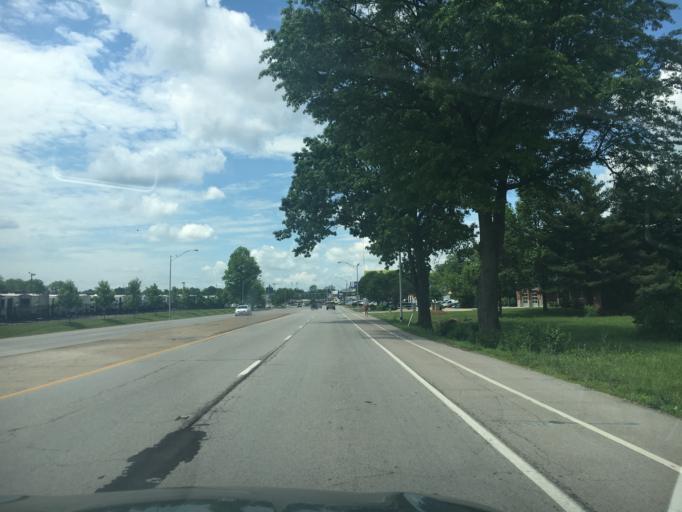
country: US
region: Kentucky
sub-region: Fayette County
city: Lexington-Fayette
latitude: 38.0700
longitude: -84.4669
